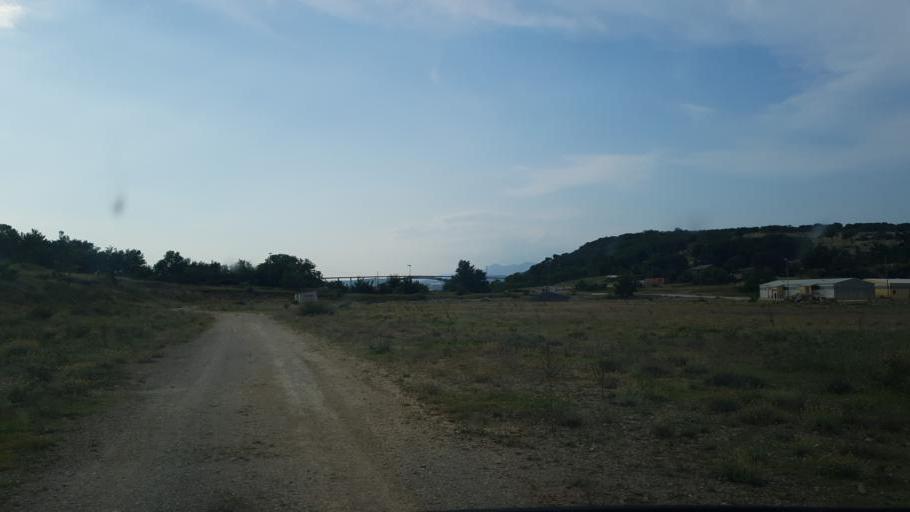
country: HR
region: Primorsko-Goranska
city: Omisalj
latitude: 45.2315
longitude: 14.5813
